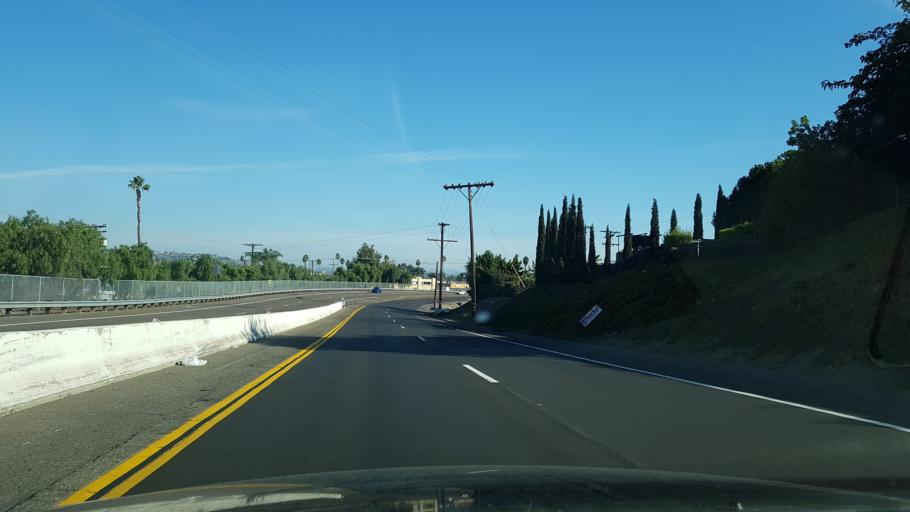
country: US
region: California
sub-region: San Diego County
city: Oceanside
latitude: 33.2103
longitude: -117.3513
